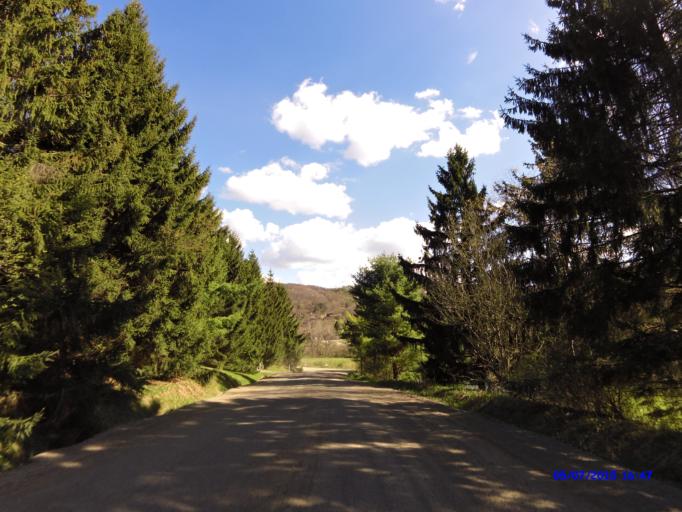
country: US
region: New York
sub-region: Cattaraugus County
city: Little Valley
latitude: 42.2774
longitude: -78.6981
